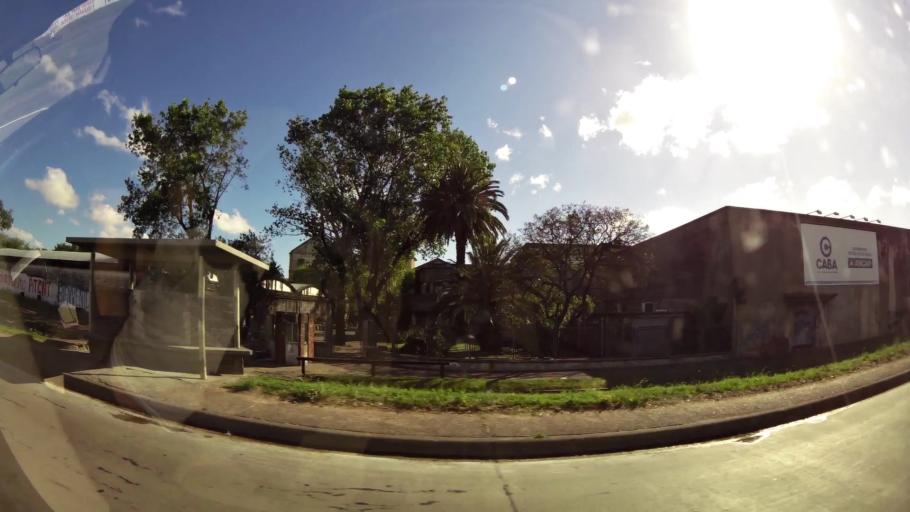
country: UY
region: Montevideo
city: Montevideo
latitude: -34.8711
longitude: -56.2183
